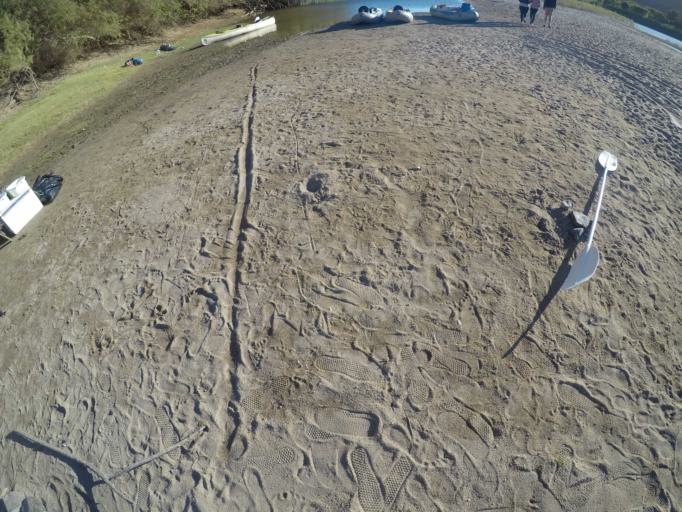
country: ZA
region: Northern Cape
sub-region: Namakwa District Municipality
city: Port Nolloth
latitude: -28.7050
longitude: 17.4734
